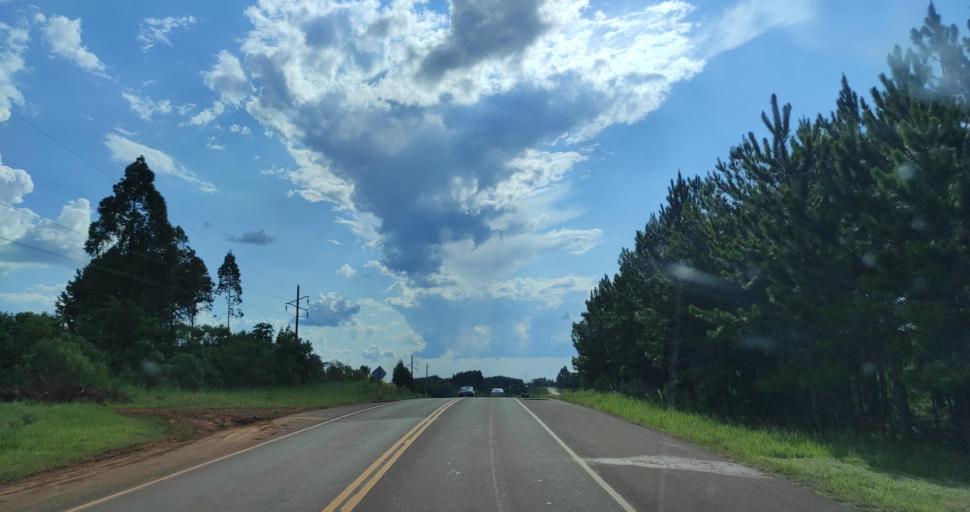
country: AR
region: Misiones
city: Bernardo de Irigoyen
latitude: -26.2950
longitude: -53.7800
